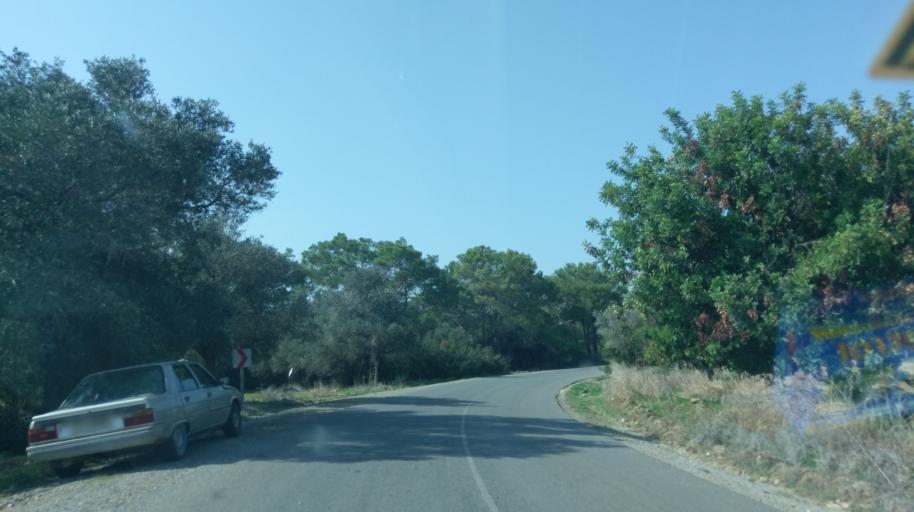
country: CY
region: Lefkosia
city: Morfou
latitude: 35.3027
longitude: 33.0085
